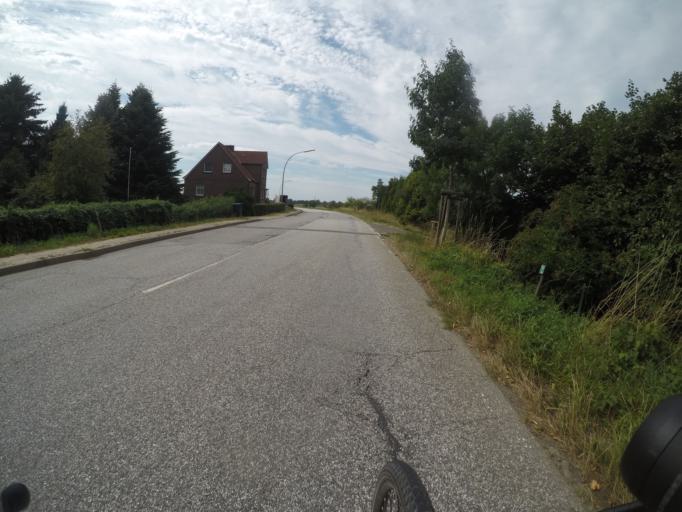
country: DE
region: Hamburg
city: Bergedorf
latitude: 53.4678
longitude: 10.1707
